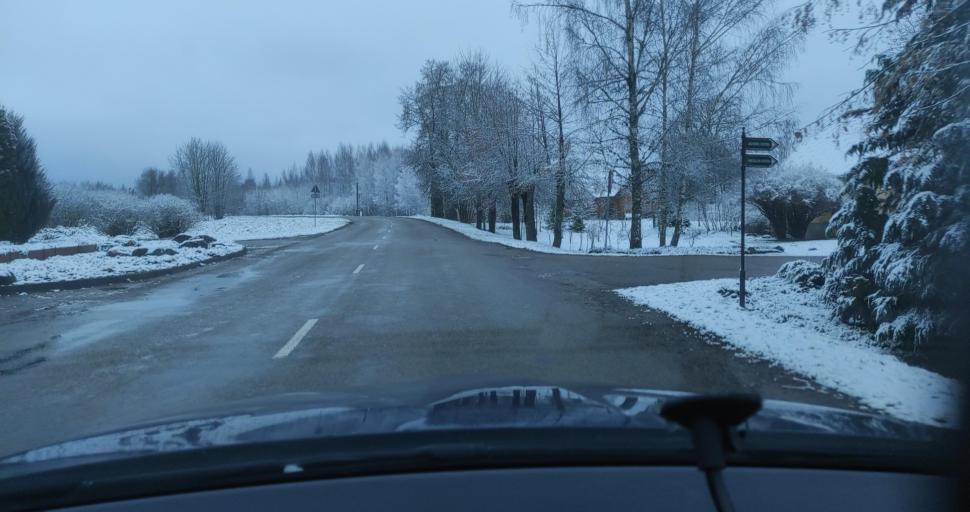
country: LV
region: Skrunda
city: Skrunda
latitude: 56.8738
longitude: 22.2385
